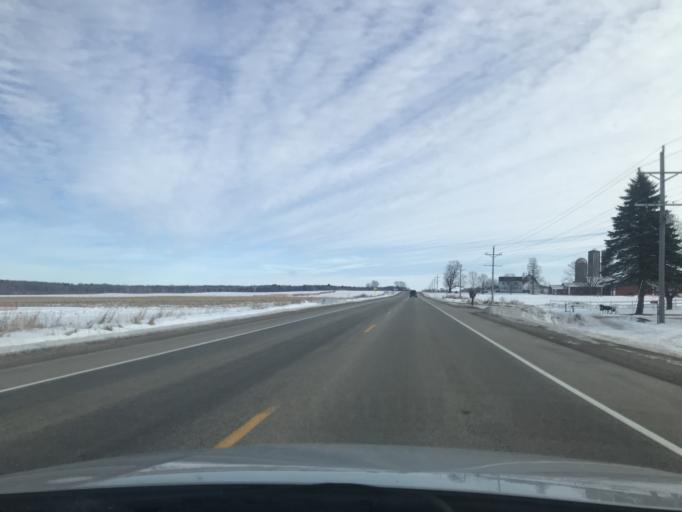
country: US
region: Wisconsin
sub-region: Oconto County
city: Gillett
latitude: 44.8958
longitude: -88.2298
